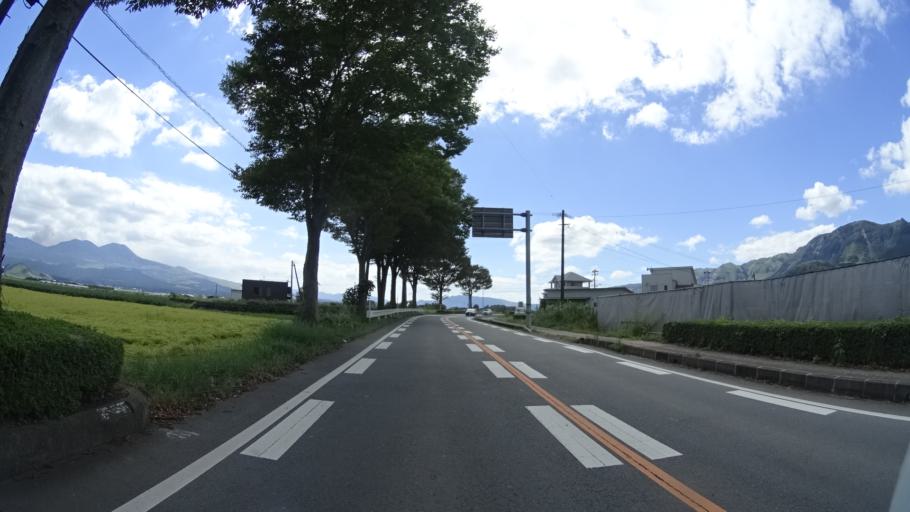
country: JP
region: Kumamoto
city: Aso
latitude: 32.9697
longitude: 131.0471
